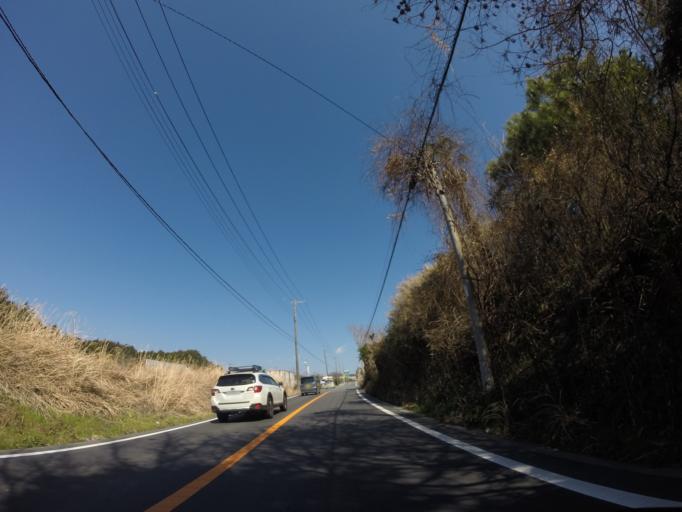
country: JP
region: Shizuoka
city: Numazu
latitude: 35.1397
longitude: 138.8367
